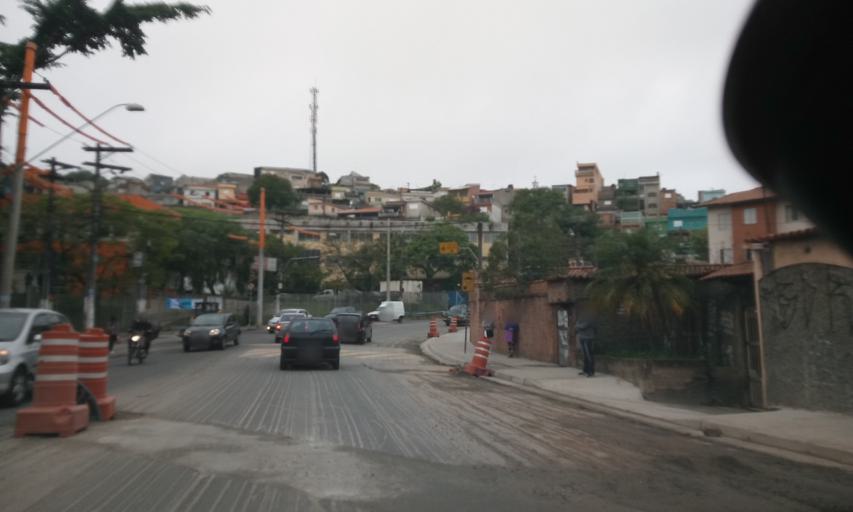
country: BR
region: Sao Paulo
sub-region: Sao Bernardo Do Campo
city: Sao Bernardo do Campo
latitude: -23.7069
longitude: -46.5216
